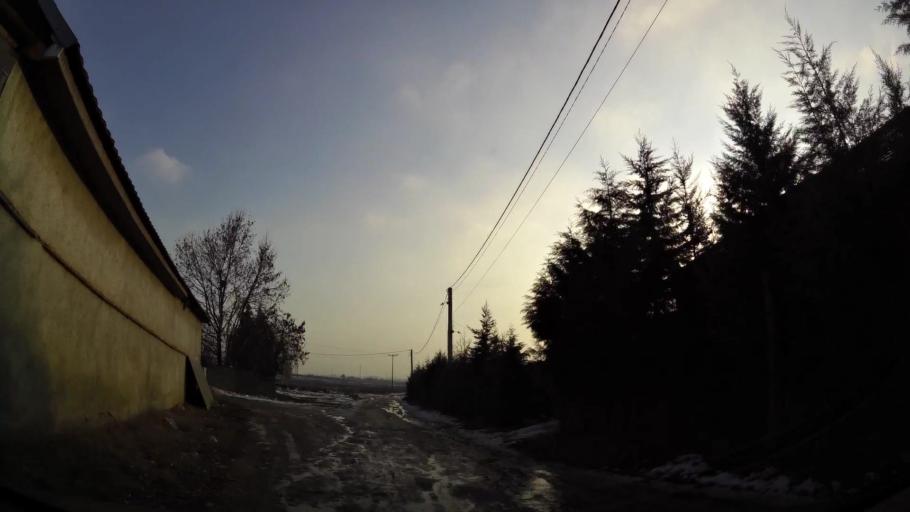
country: MK
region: Aracinovo
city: Arachinovo
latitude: 42.0201
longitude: 21.5676
